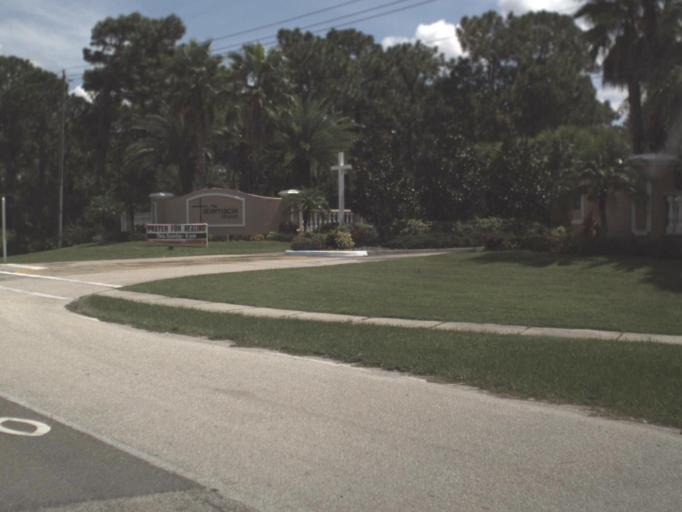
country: US
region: Florida
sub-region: Sarasota County
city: Desoto Lakes
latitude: 27.3883
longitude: -82.4855
